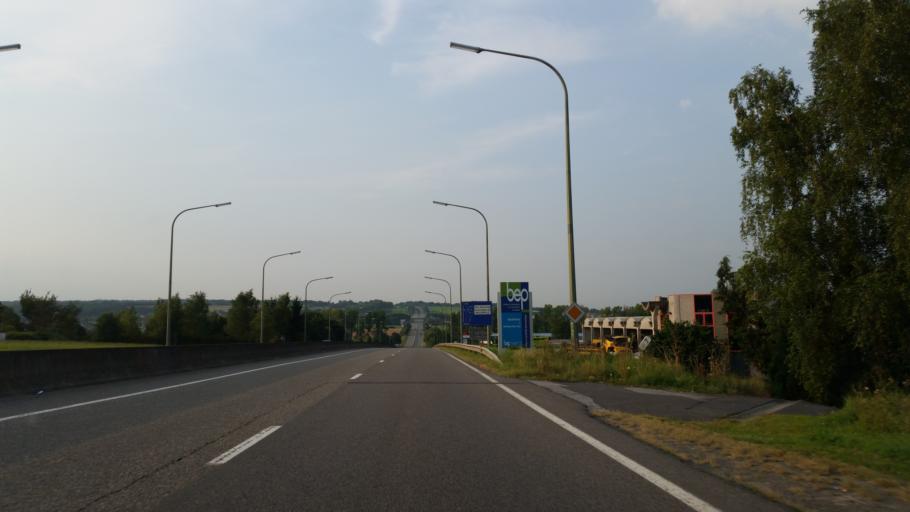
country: BE
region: Wallonia
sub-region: Province du Luxembourg
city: Marche-en-Famenne
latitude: 50.2786
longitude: 5.3482
